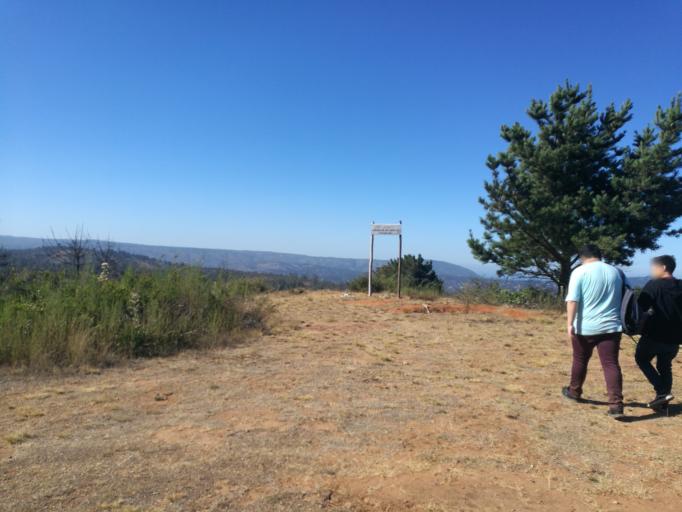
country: CL
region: Valparaiso
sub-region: Provincia de Valparaiso
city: Valparaiso
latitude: -33.0711
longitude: -71.6519
